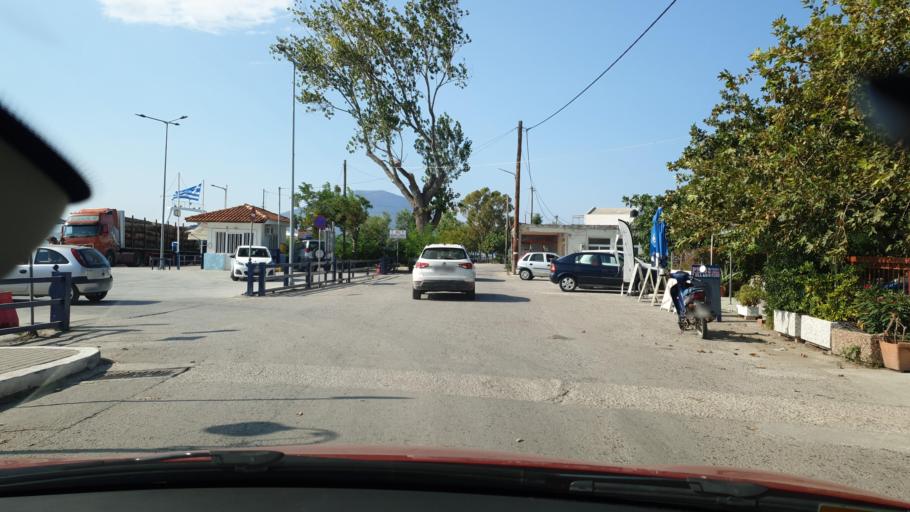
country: GR
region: Central Greece
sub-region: Nomos Evvoias
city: Oreoi
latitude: 38.9347
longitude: 23.0350
